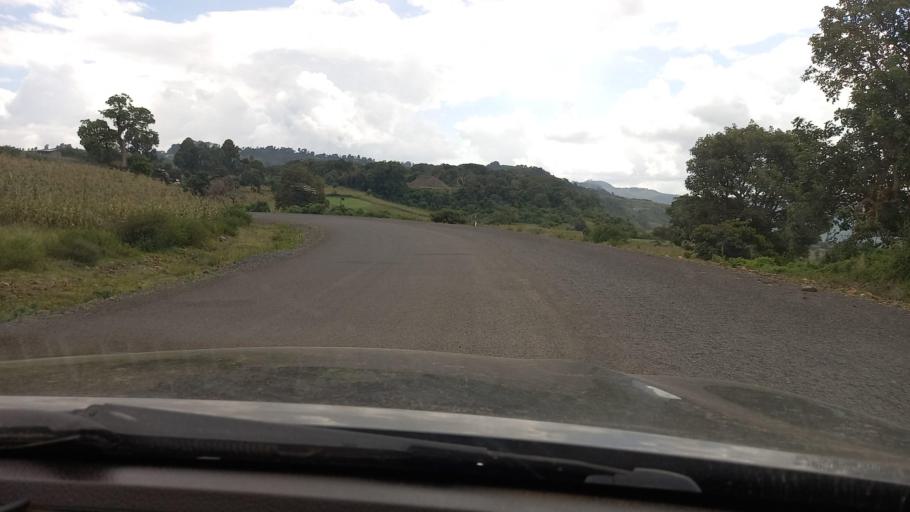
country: ET
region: Southern Nations, Nationalities, and People's Region
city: Mizan Teferi
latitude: 6.2134
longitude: 35.6146
